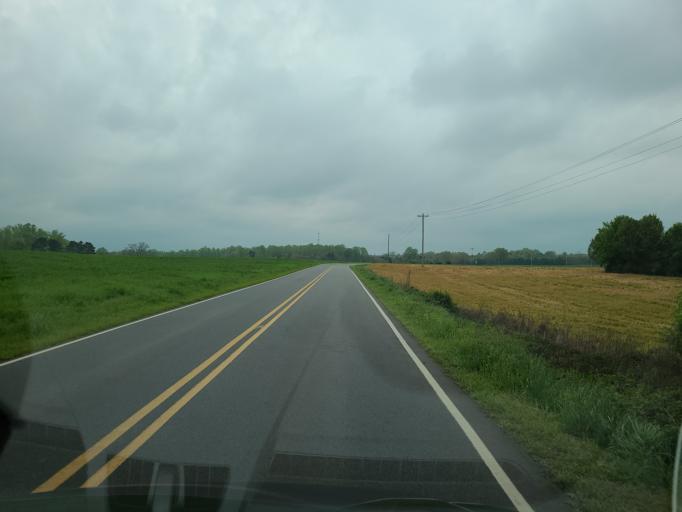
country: US
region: North Carolina
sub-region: Gaston County
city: Cherryville
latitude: 35.4361
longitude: -81.3893
